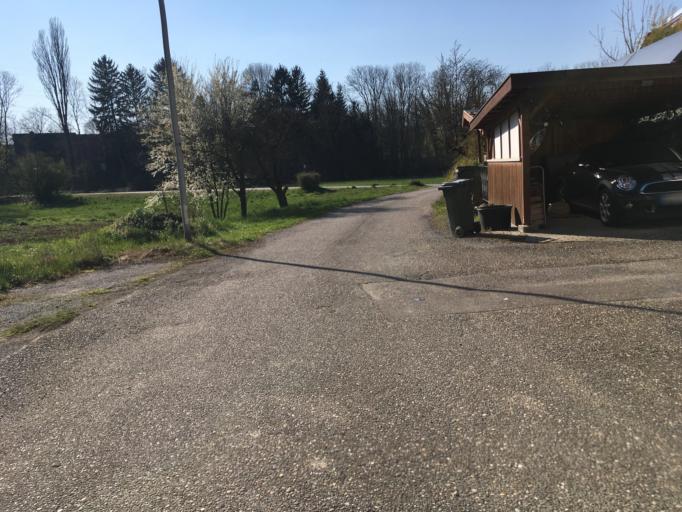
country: DE
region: Baden-Wuerttemberg
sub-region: Regierungsbezirk Stuttgart
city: Talheim
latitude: 49.0966
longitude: 9.1801
